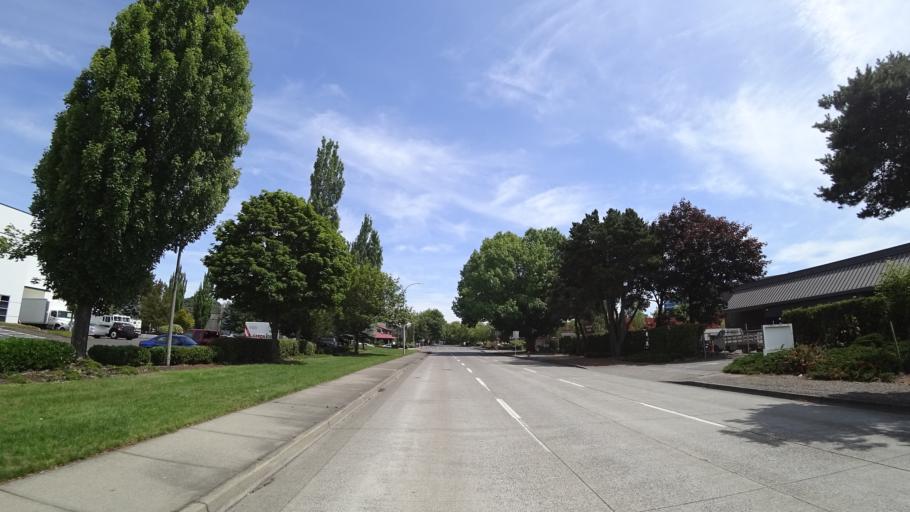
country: US
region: Oregon
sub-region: Multnomah County
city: Portland
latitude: 45.5584
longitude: -122.7040
